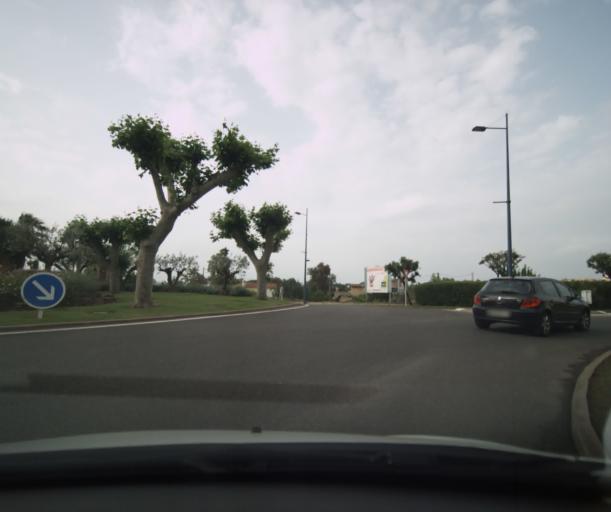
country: FR
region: Provence-Alpes-Cote d'Azur
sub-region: Departement du Var
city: Carqueiranne
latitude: 43.0927
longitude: 6.0766
